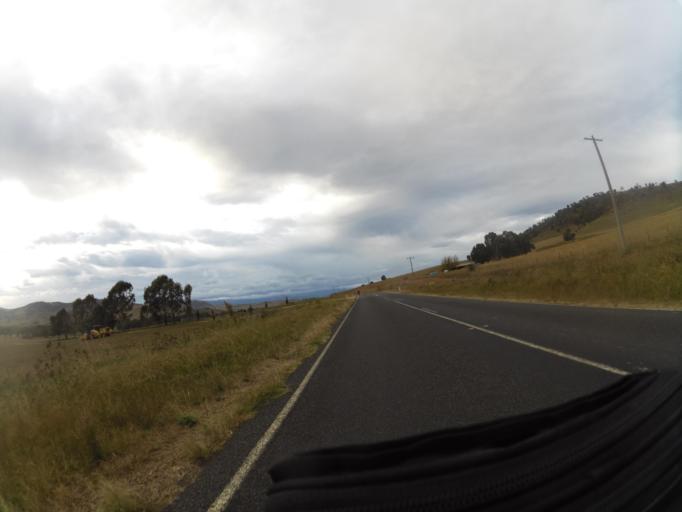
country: AU
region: New South Wales
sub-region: Snowy River
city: Jindabyne
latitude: -36.0776
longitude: 147.9730
